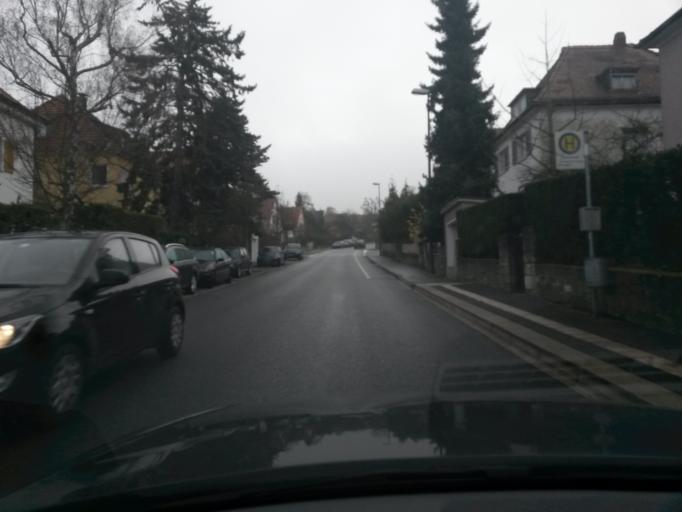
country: DE
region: Bavaria
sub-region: Regierungsbezirk Unterfranken
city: Wuerzburg
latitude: 49.7839
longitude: 9.9537
